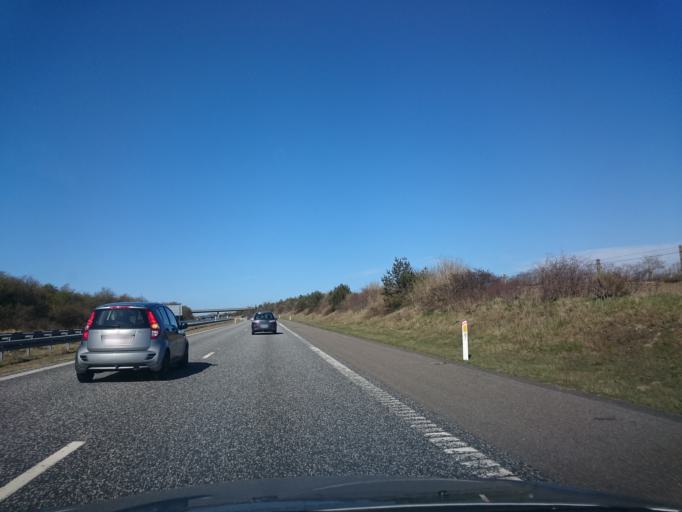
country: DK
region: North Denmark
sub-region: Hjorring Kommune
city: Hjorring
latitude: 57.5237
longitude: 10.0110
